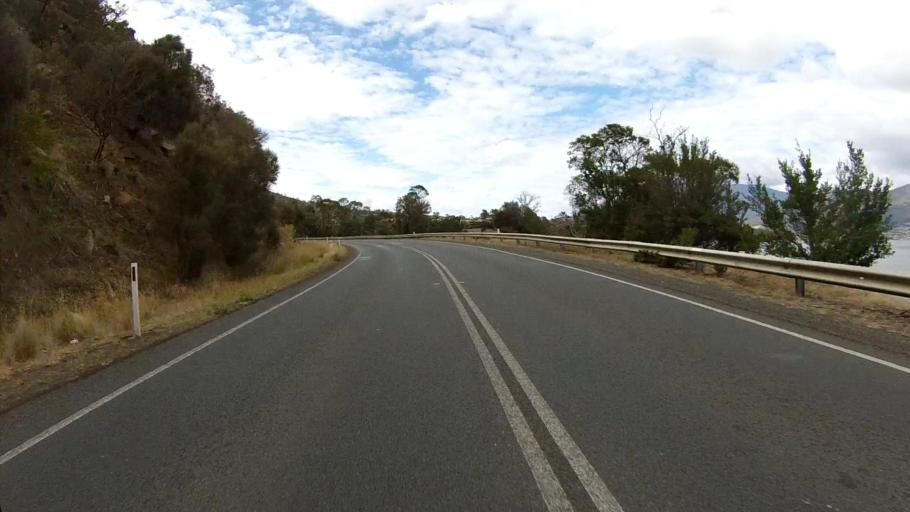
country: AU
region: Tasmania
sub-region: Brighton
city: Old Beach
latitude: -42.7868
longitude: 147.2912
